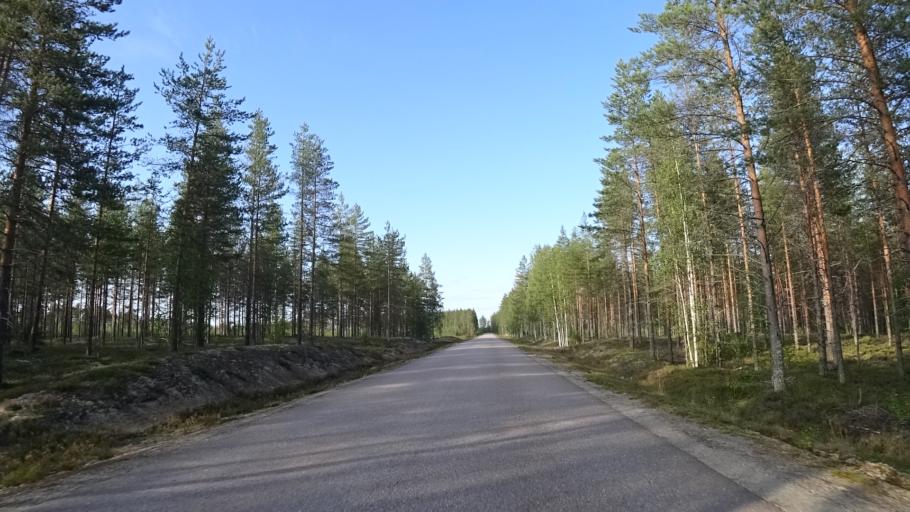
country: FI
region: North Karelia
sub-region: Joensuu
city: Eno
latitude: 63.0796
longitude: 30.5830
